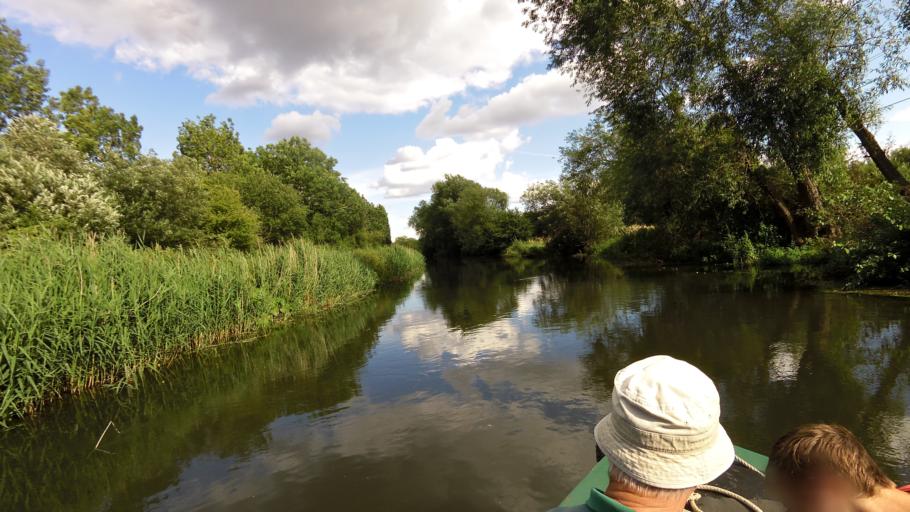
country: GB
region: England
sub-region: West Berkshire
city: Thatcham
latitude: 51.3950
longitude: -1.2800
